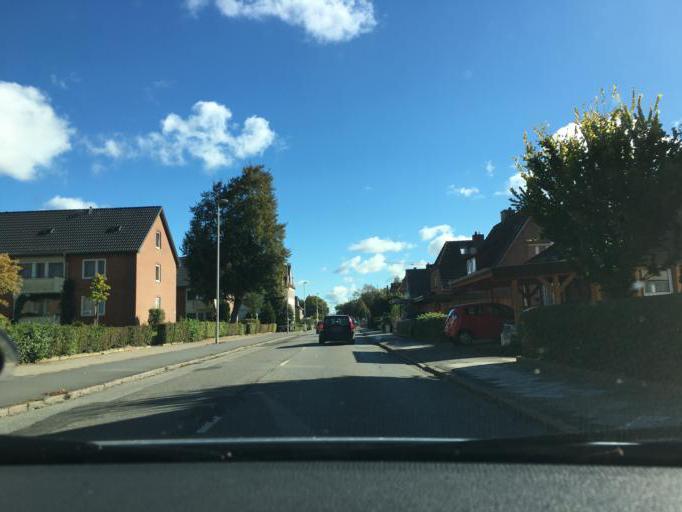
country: DE
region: Schleswig-Holstein
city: Kronshagen
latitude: 54.3321
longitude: 10.0787
